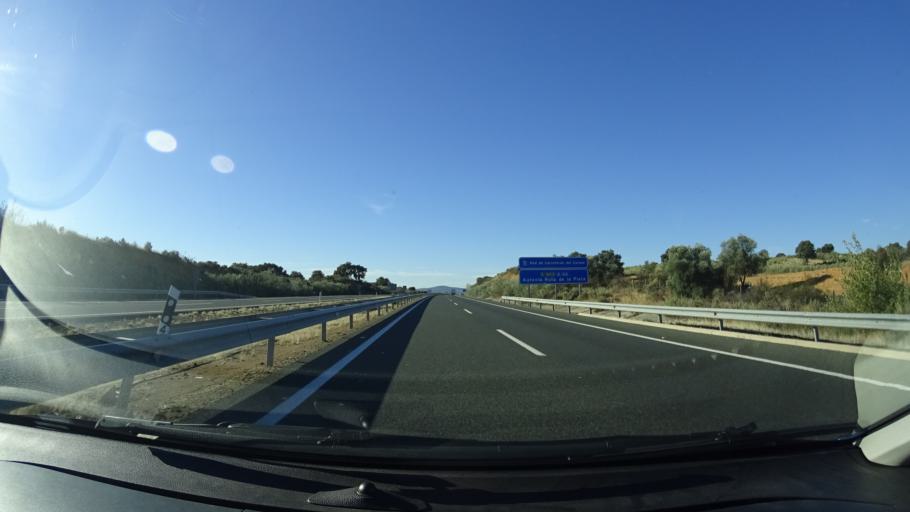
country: ES
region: Extremadura
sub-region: Provincia de Badajoz
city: Monesterio
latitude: 38.0222
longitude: -6.2237
